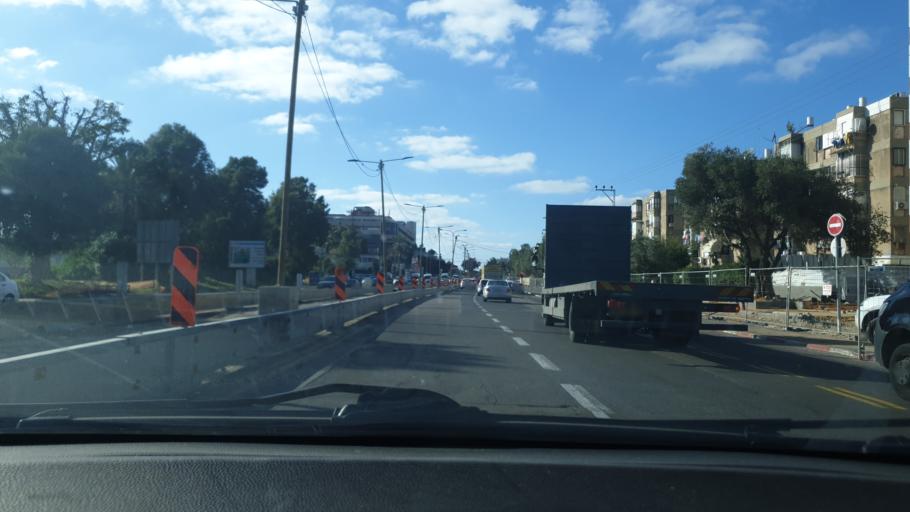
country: IL
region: Tel Aviv
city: Yafo
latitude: 32.0398
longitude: 34.7763
